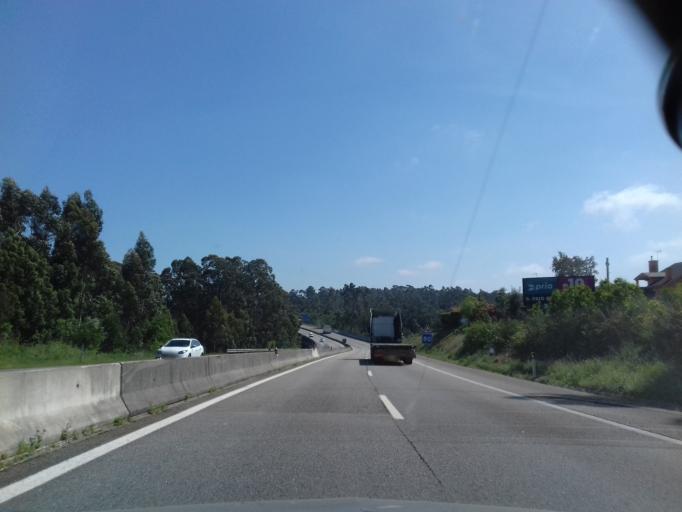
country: PT
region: Aveiro
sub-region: Espinho
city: Souto
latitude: 40.9842
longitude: -8.6125
